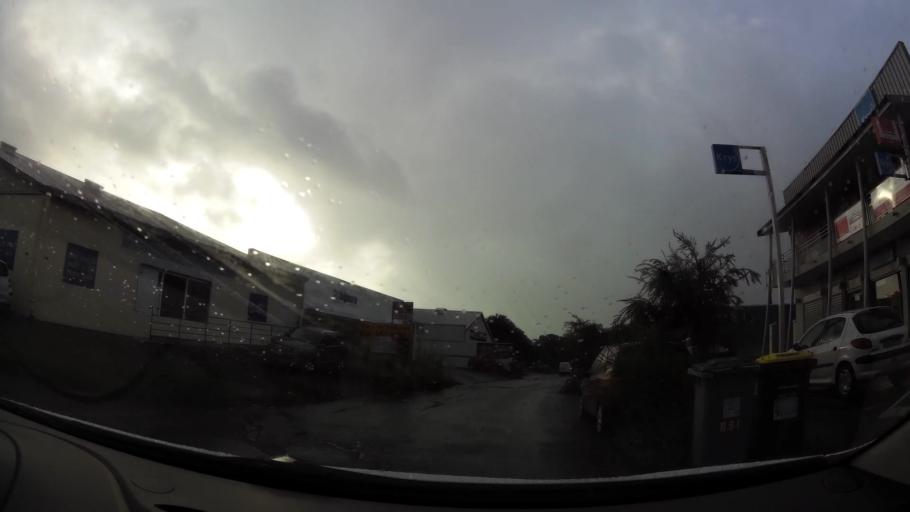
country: RE
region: Reunion
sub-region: Reunion
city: Saint-Andre
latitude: -20.9611
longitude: 55.6609
